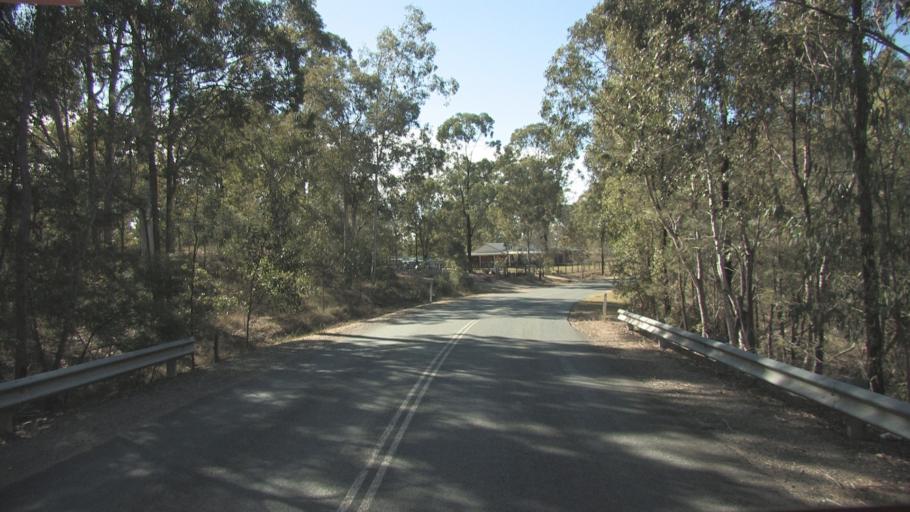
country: AU
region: Queensland
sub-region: Ipswich
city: Springfield Lakes
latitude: -27.7109
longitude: 152.9301
